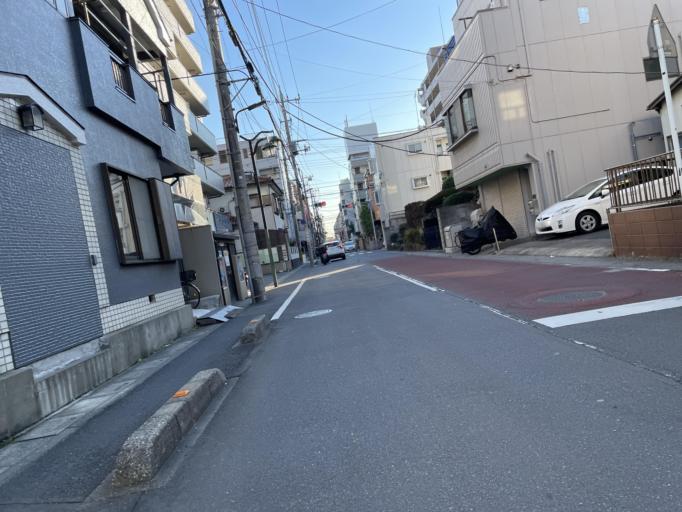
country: JP
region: Saitama
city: Soka
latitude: 35.8297
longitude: 139.8014
